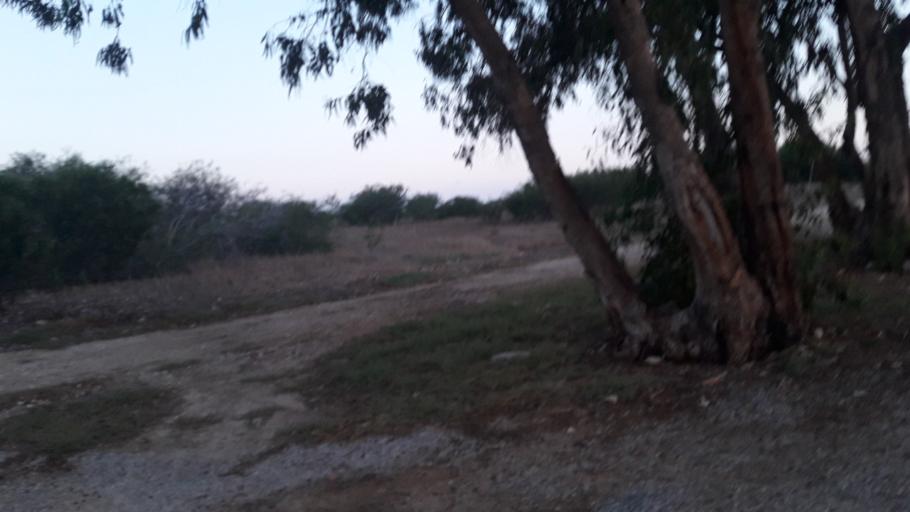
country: CY
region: Ammochostos
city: Famagusta
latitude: 35.1815
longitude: 33.9015
